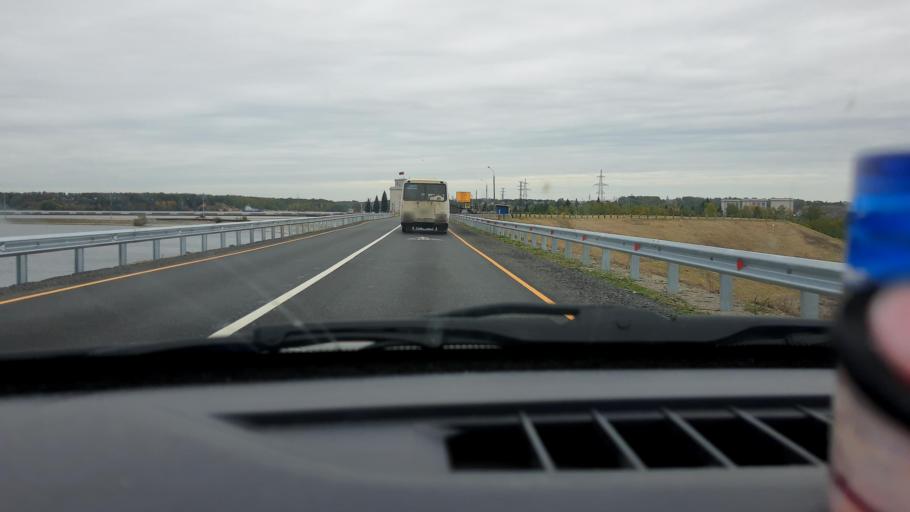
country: RU
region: Nizjnij Novgorod
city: Zavolzh'ye
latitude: 56.6743
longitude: 43.4074
